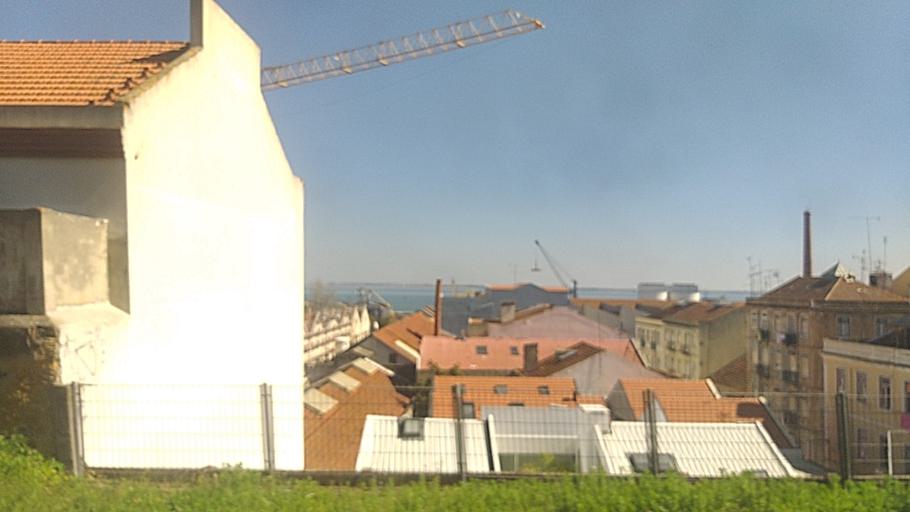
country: PT
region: Lisbon
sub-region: Lisbon
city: Lisbon
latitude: 38.7395
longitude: -9.1056
